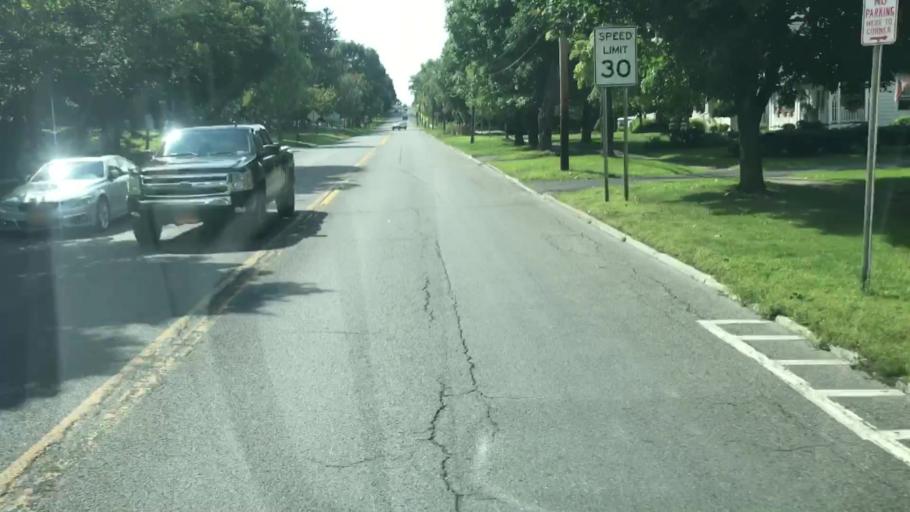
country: US
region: New York
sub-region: Onondaga County
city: Skaneateles
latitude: 42.9447
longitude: -76.4373
